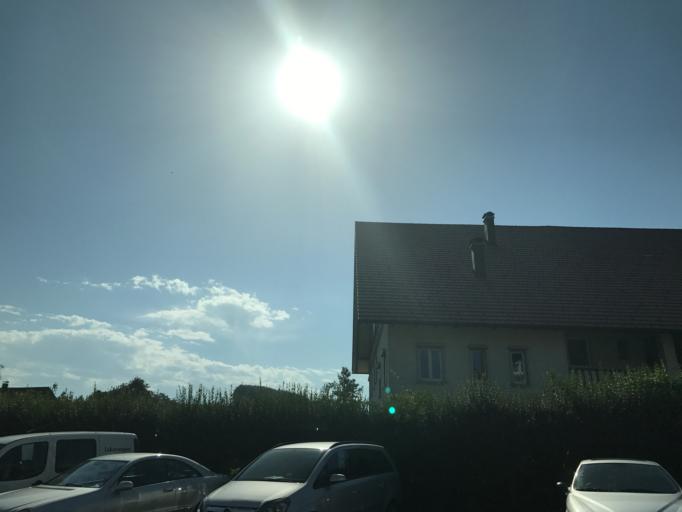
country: DE
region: Baden-Wuerttemberg
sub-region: Tuebingen Region
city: Wangen im Allgau
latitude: 47.7064
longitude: 9.8492
